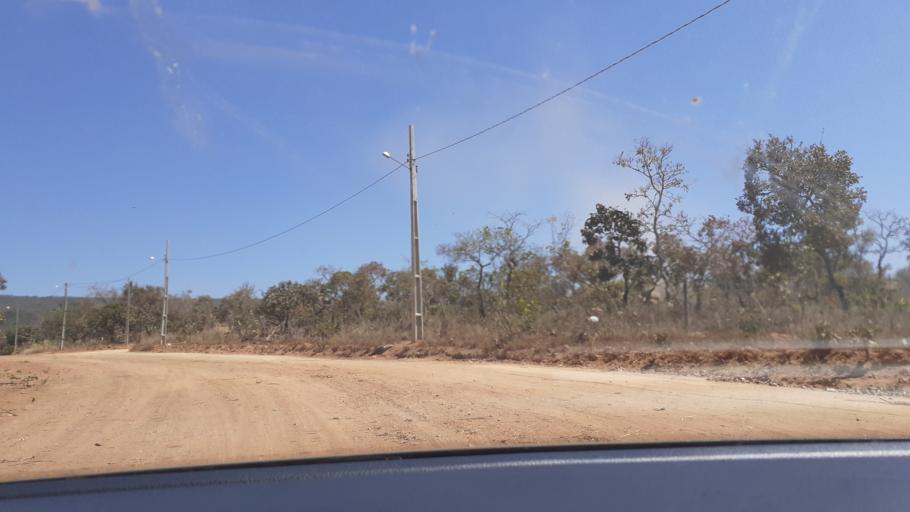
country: BR
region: Goias
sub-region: Caldas Novas
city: Caldas Novas
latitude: -17.7441
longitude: -48.6554
